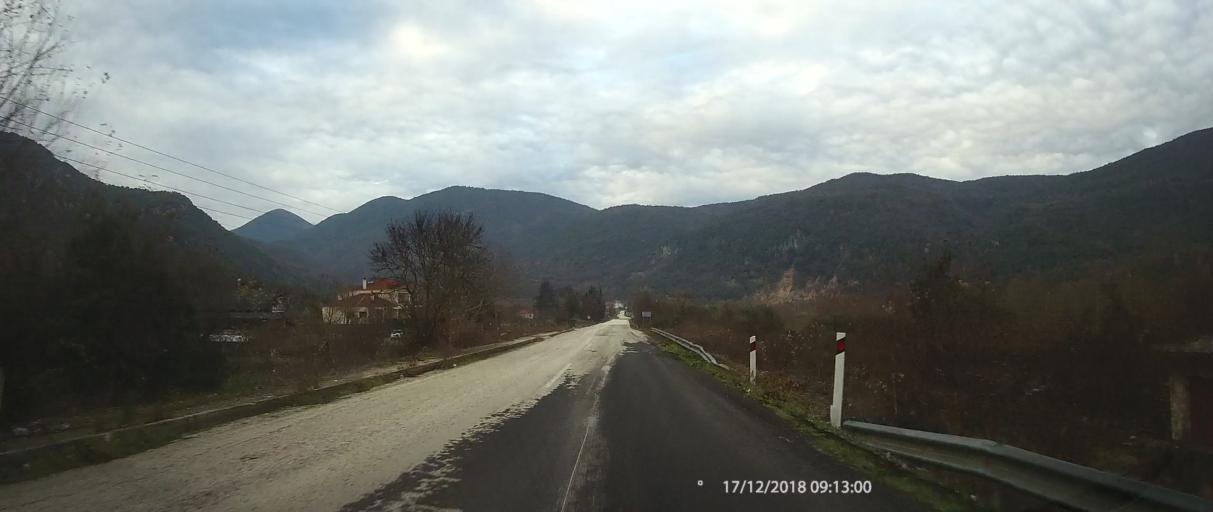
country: GR
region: Epirus
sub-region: Nomos Ioanninon
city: Kalpaki
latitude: 39.9764
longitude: 20.6627
